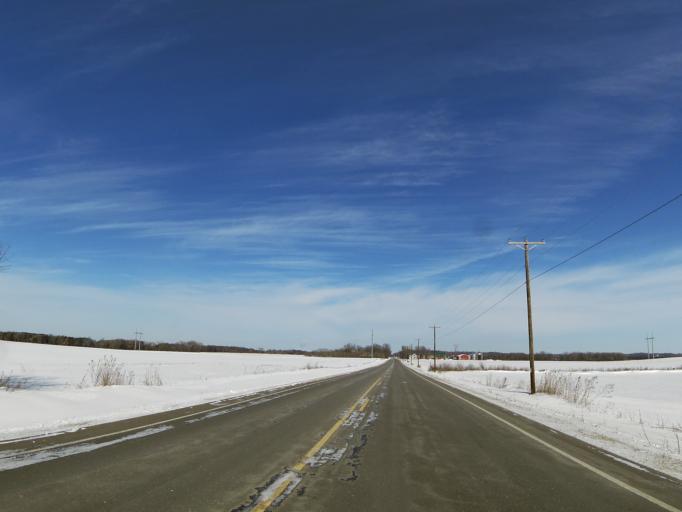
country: US
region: Minnesota
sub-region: Washington County
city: Afton
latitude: 44.8508
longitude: -92.7312
